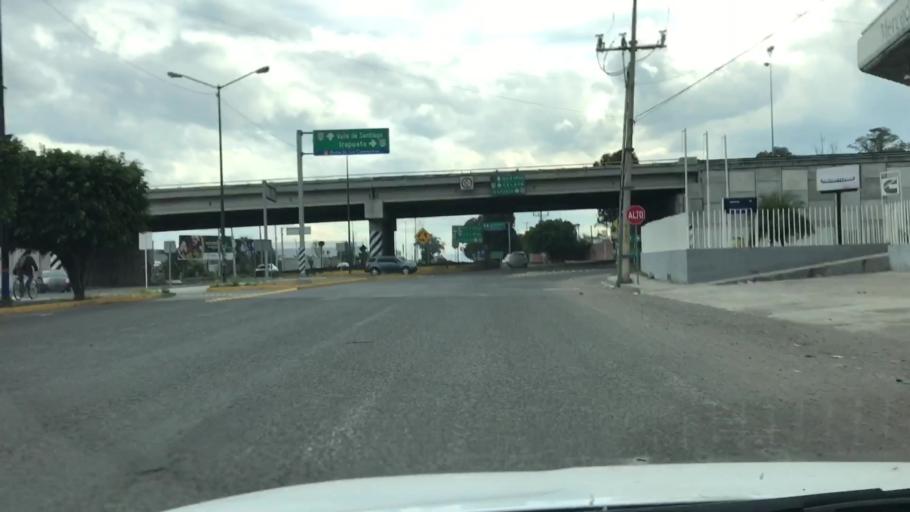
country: MX
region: Guanajuato
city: Salamanca
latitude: 20.5417
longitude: -101.2051
